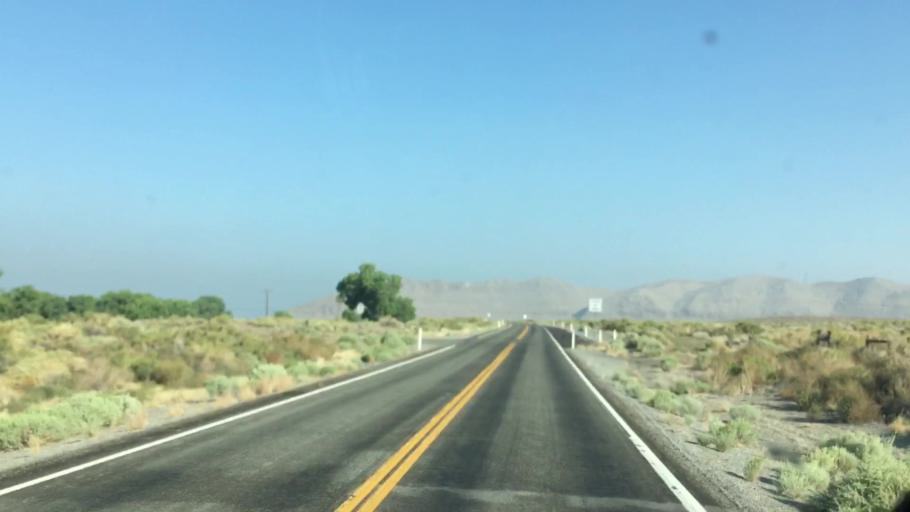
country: US
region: Nevada
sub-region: Lyon County
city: Fernley
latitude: 39.8474
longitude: -119.3689
